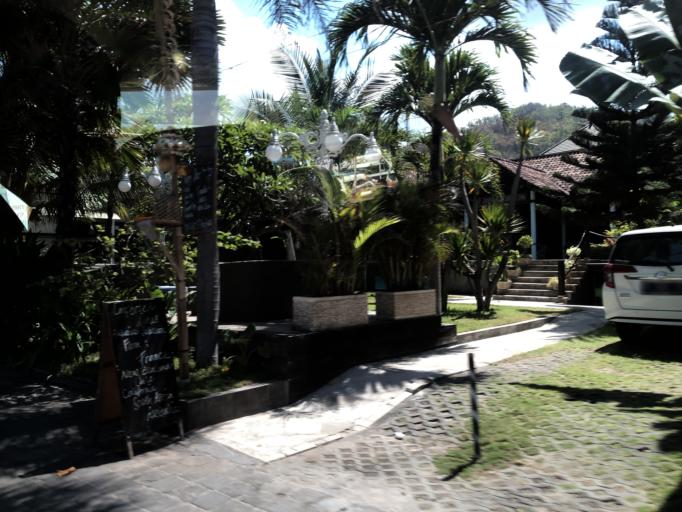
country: ID
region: Bali
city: Padangbai
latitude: -8.5306
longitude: 115.5096
